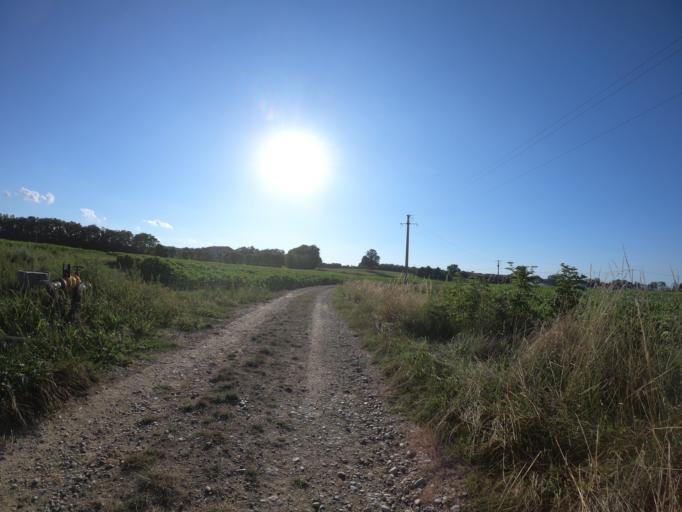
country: FR
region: Midi-Pyrenees
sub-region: Departement de l'Ariege
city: La Tour-du-Crieu
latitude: 43.1023
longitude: 1.7313
